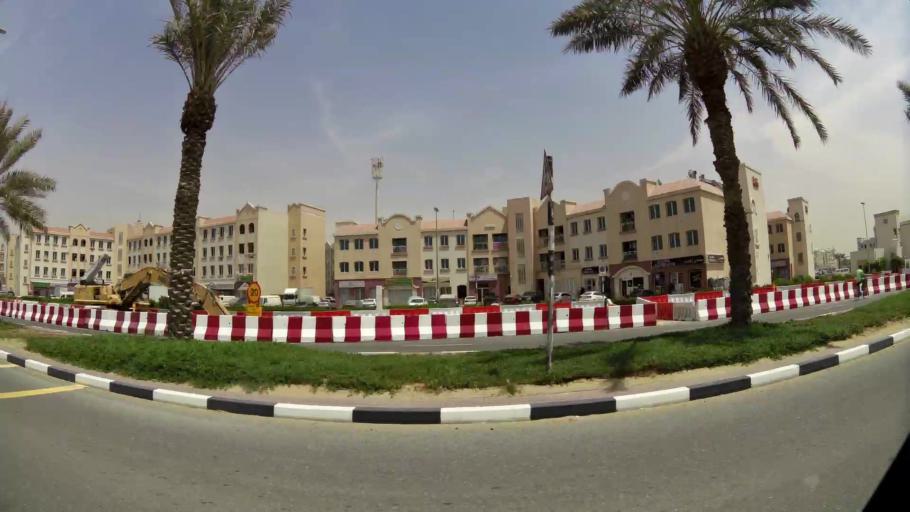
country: AE
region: Ash Shariqah
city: Sharjah
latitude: 25.1744
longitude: 55.4002
